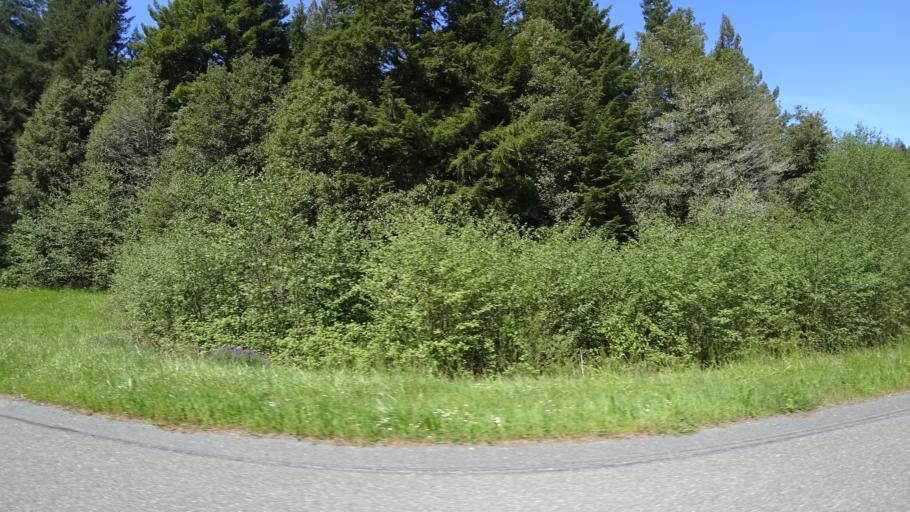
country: US
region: California
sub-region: Del Norte County
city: Bertsch-Oceanview
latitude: 41.4403
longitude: -124.0215
